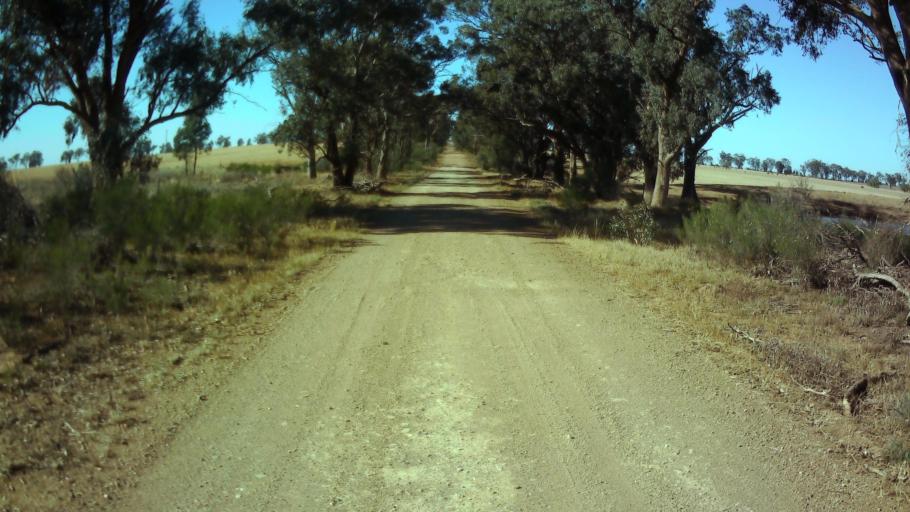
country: AU
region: New South Wales
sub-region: Weddin
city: Grenfell
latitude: -33.8929
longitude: 147.8801
